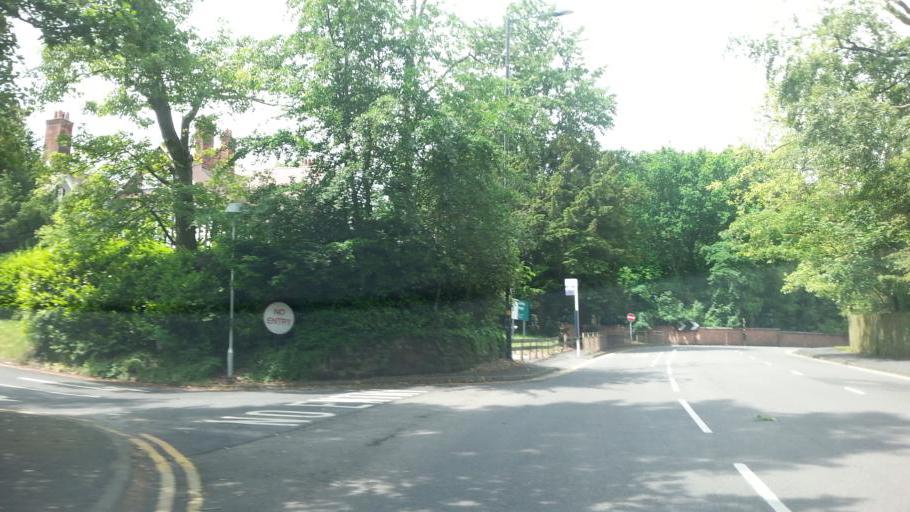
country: GB
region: England
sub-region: City and Borough of Birmingham
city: Birmingham
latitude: 52.4567
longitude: -1.9133
